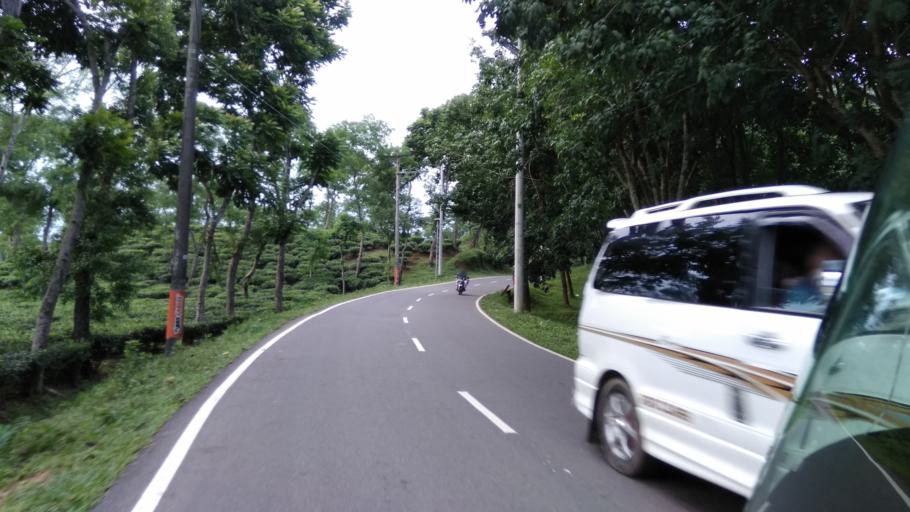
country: IN
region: Tripura
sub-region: Dhalai
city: Kamalpur
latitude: 24.3005
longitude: 91.7547
